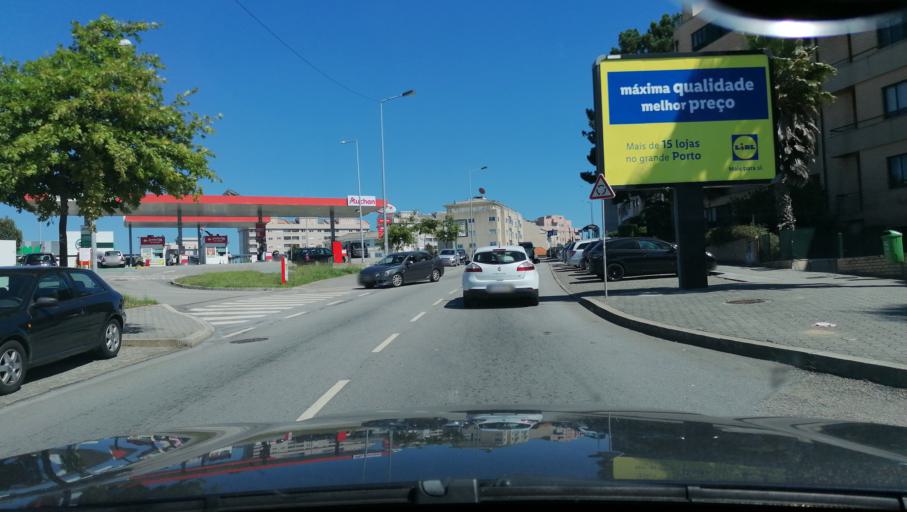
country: PT
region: Porto
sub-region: Vila Nova de Gaia
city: Canidelo
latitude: 41.1308
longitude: -8.6473
